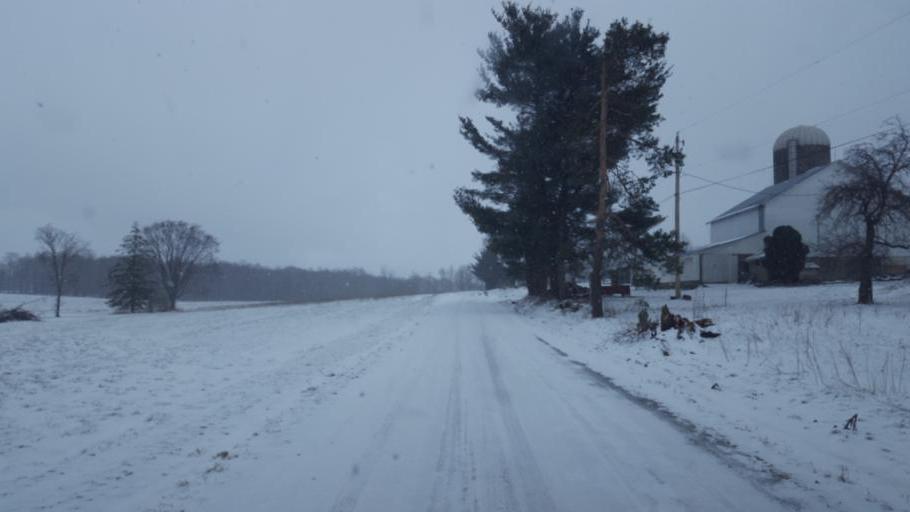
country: US
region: Pennsylvania
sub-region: Crawford County
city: Cochranton
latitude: 41.4365
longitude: -80.0901
